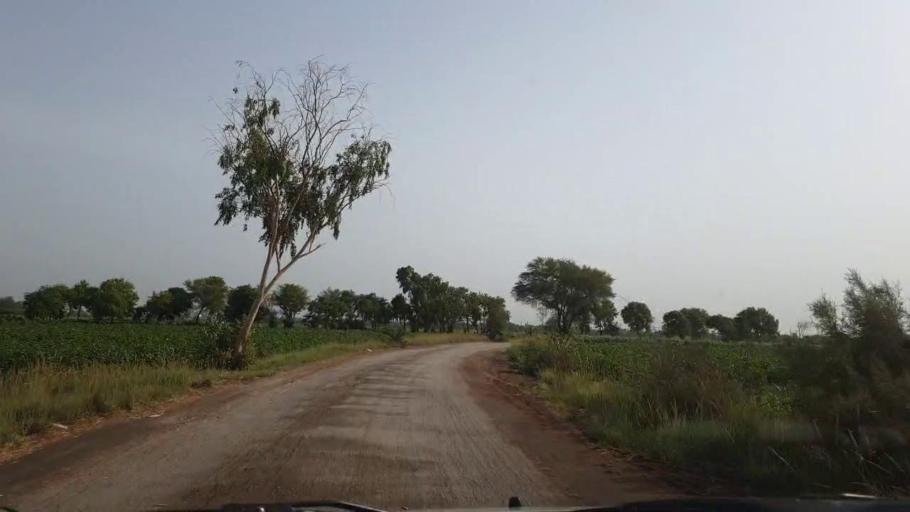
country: PK
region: Sindh
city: Nawabshah
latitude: 26.2218
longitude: 68.4049
